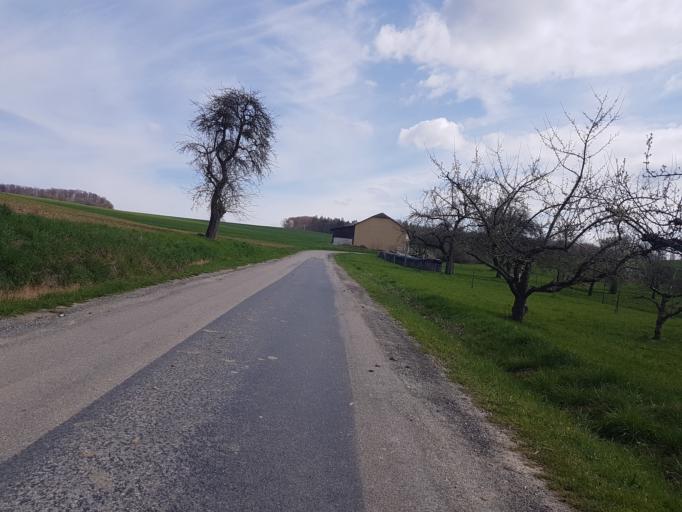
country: DE
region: Baden-Wuerttemberg
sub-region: Regierungsbezirk Stuttgart
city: Forchtenberg
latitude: 49.3697
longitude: 9.5479
